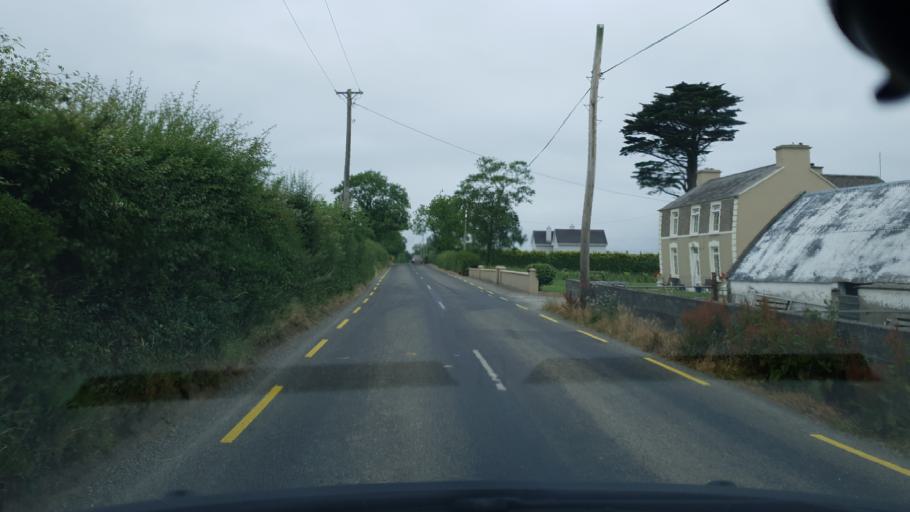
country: IE
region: Munster
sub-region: Ciarrai
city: Tralee
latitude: 52.1618
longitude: -9.6497
